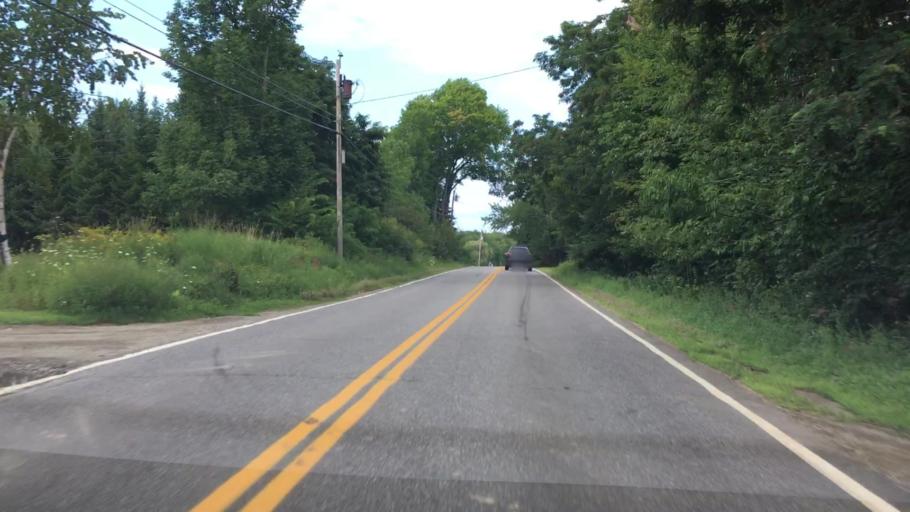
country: US
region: Maine
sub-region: Waldo County
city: Belfast
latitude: 44.3668
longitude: -69.0399
